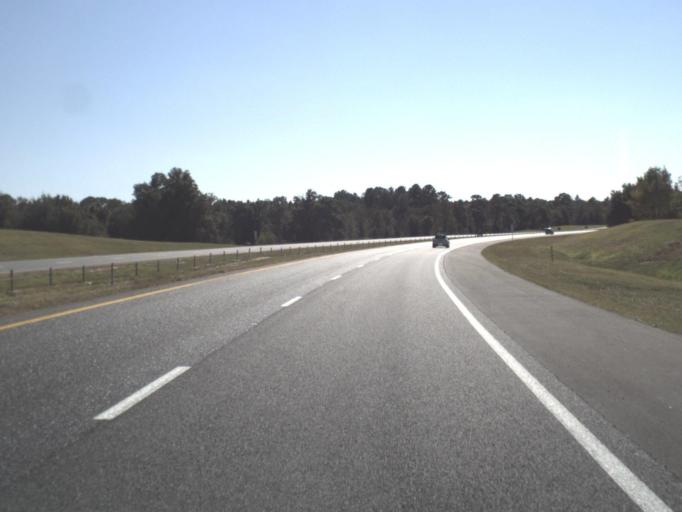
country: US
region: Florida
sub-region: Hernando County
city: Brookridge
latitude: 28.5865
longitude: -82.4813
